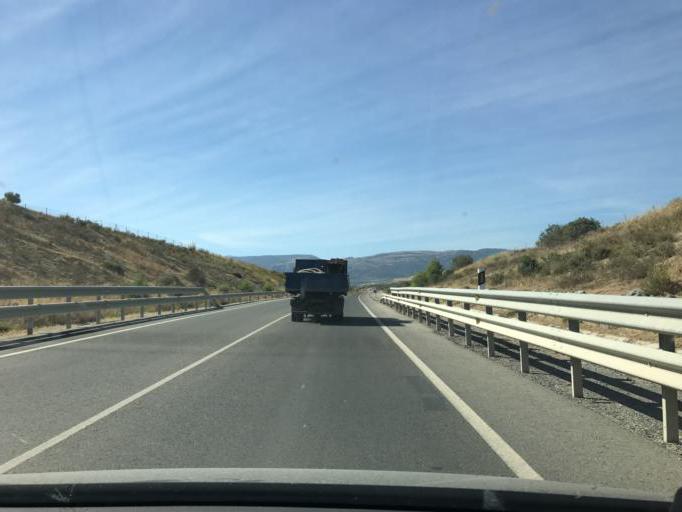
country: ES
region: Andalusia
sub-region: Province of Cordoba
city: Baena
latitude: 37.6081
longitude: -4.3017
